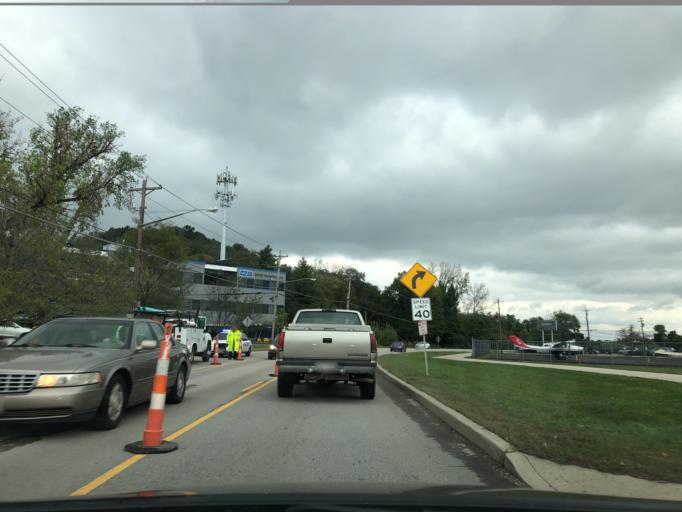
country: US
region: Kentucky
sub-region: Campbell County
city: Fort Thomas
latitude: 39.1045
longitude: -84.4296
